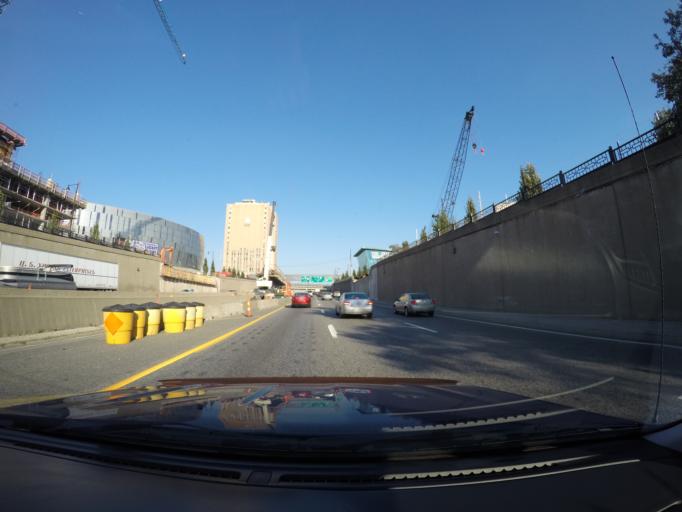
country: US
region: Missouri
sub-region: Jackson County
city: Kansas City
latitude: 39.0960
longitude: -94.5819
